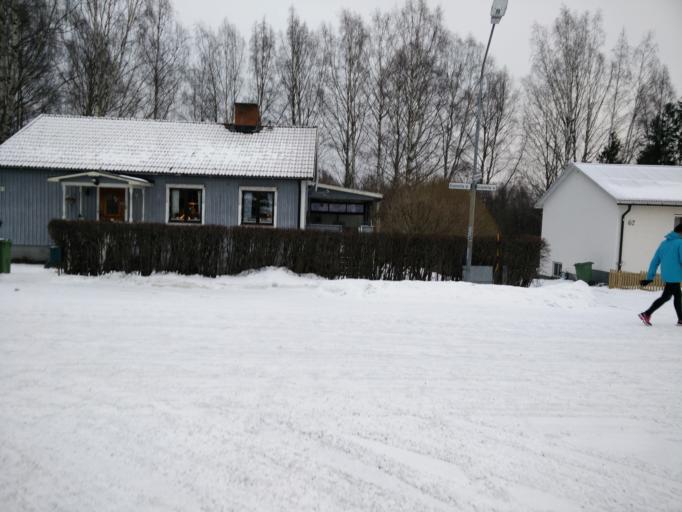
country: SE
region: Vaesternorrland
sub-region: Sundsvalls Kommun
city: Nolby
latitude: 62.2883
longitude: 17.3670
